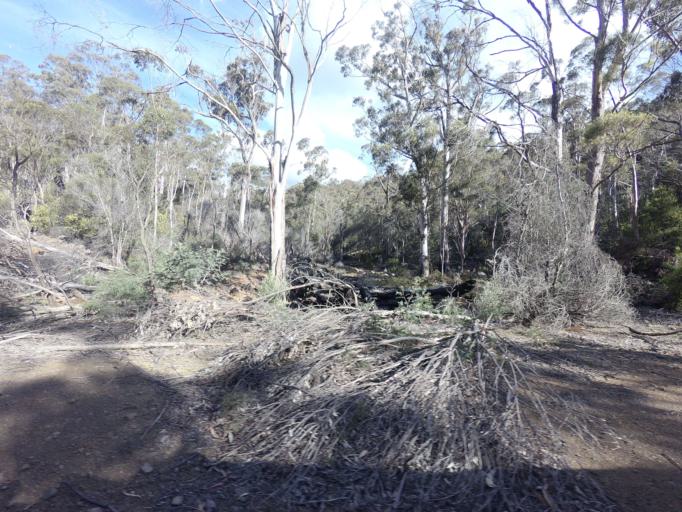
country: AU
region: Tasmania
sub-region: Break O'Day
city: St Helens
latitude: -41.8545
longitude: 148.0392
